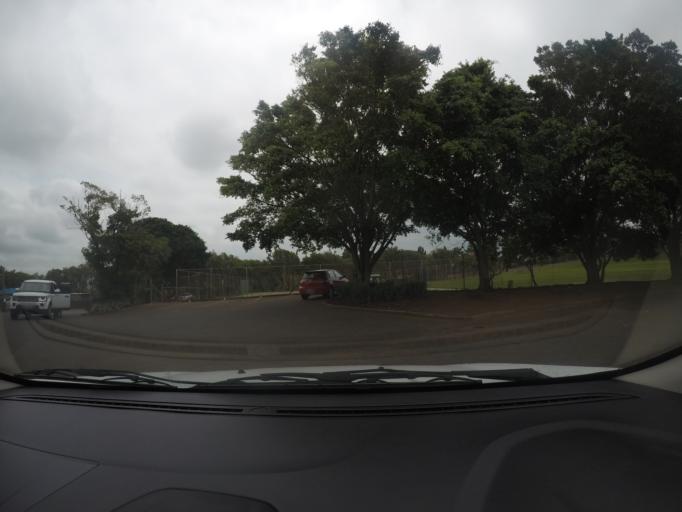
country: ZA
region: KwaZulu-Natal
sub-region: uThungulu District Municipality
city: Empangeni
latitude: -28.7530
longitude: 31.8860
